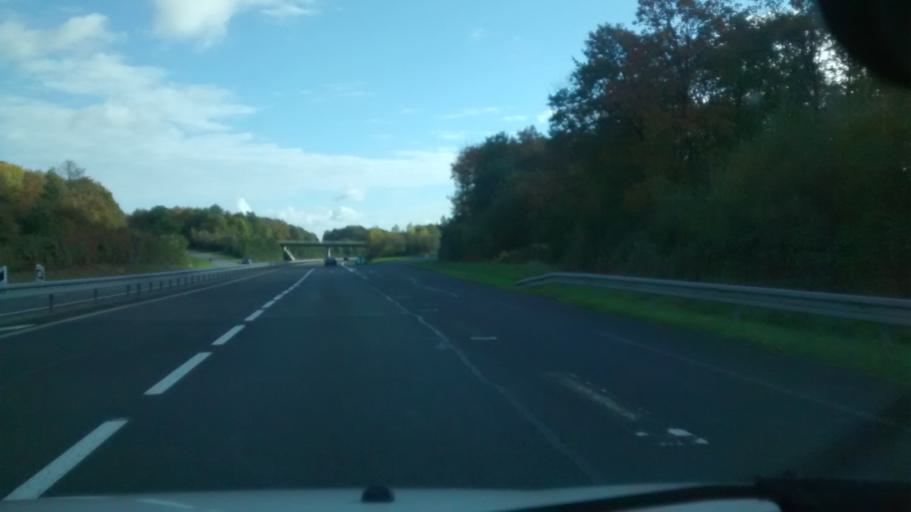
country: FR
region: Pays de la Loire
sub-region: Departement de Maine-et-Loire
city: Combree
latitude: 47.7160
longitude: -1.0159
